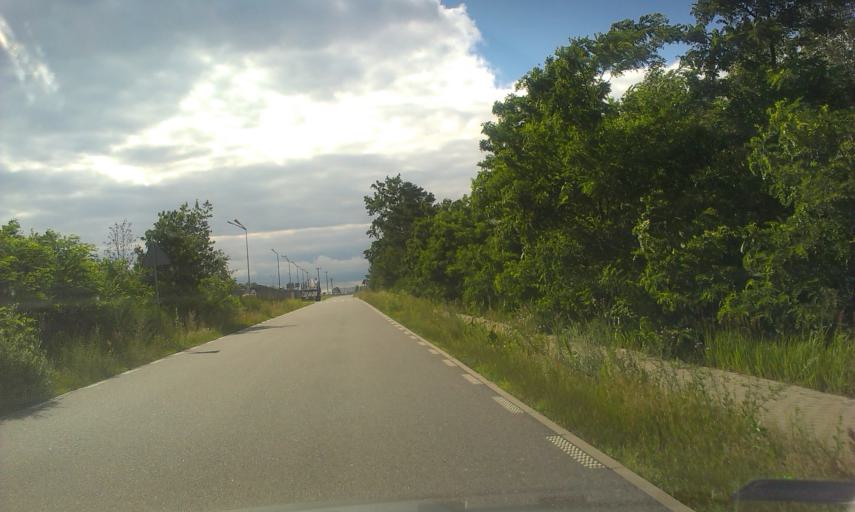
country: PL
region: Masovian Voivodeship
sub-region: Powiat zyrardowski
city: Radziejowice
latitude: 51.9697
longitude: 20.5803
